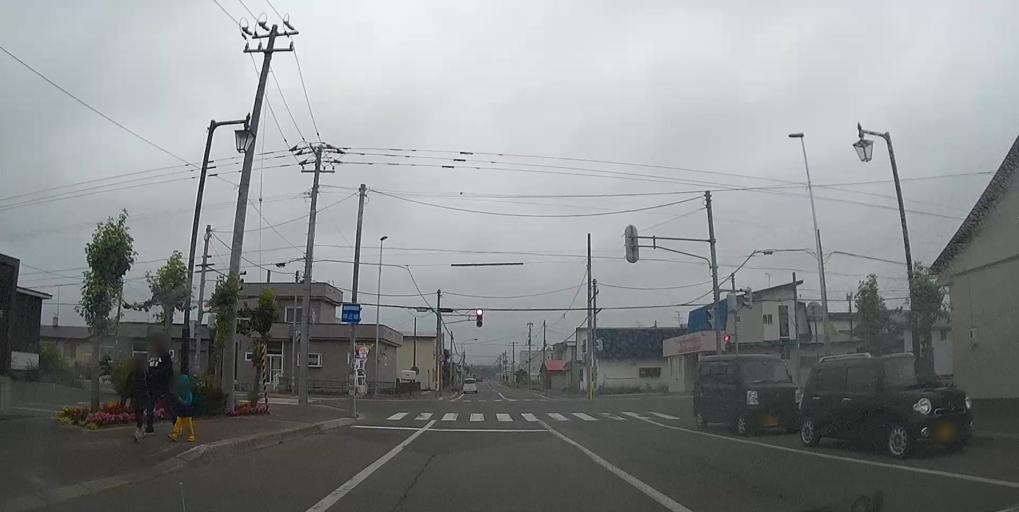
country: JP
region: Hokkaido
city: Iwanai
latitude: 42.4272
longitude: 140.0141
